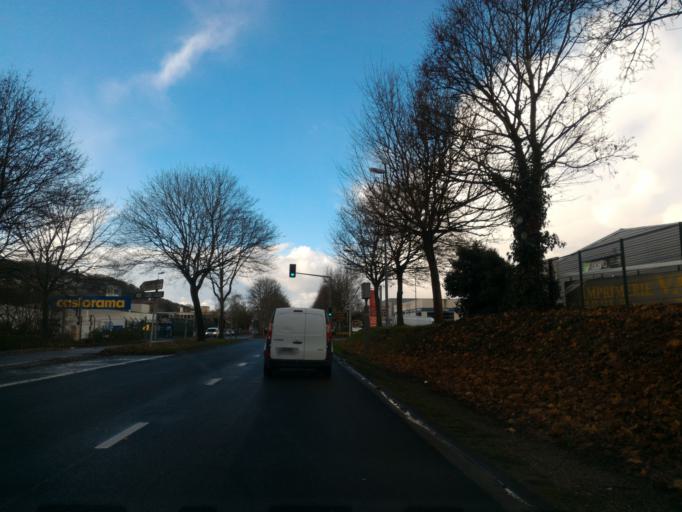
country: FR
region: Haute-Normandie
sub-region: Departement de la Seine-Maritime
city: Darnetal
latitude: 49.4365
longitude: 1.1348
